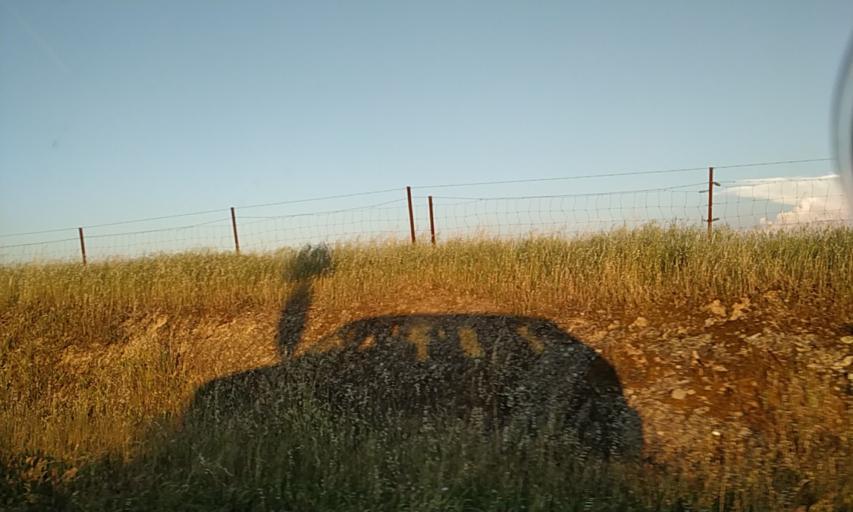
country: ES
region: Extremadura
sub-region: Provincia de Caceres
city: Salorino
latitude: 39.5308
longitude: -7.0485
